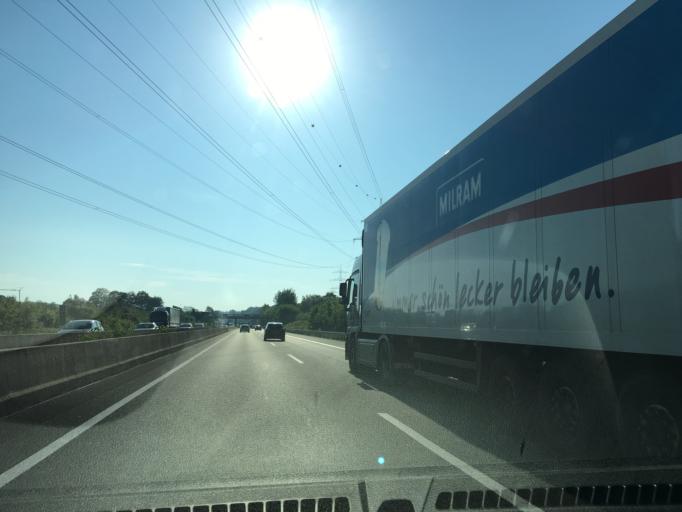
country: DE
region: Lower Saxony
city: Osnabrueck
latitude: 52.2441
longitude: 8.0450
